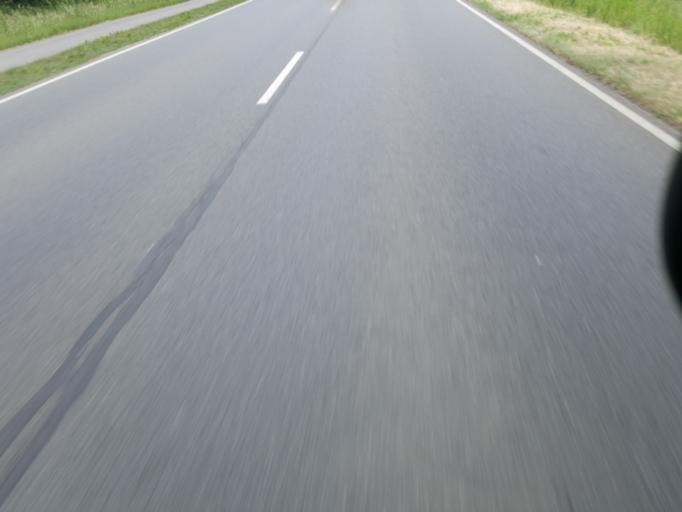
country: DE
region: Lower Saxony
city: Leese
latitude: 52.4720
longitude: 9.1406
